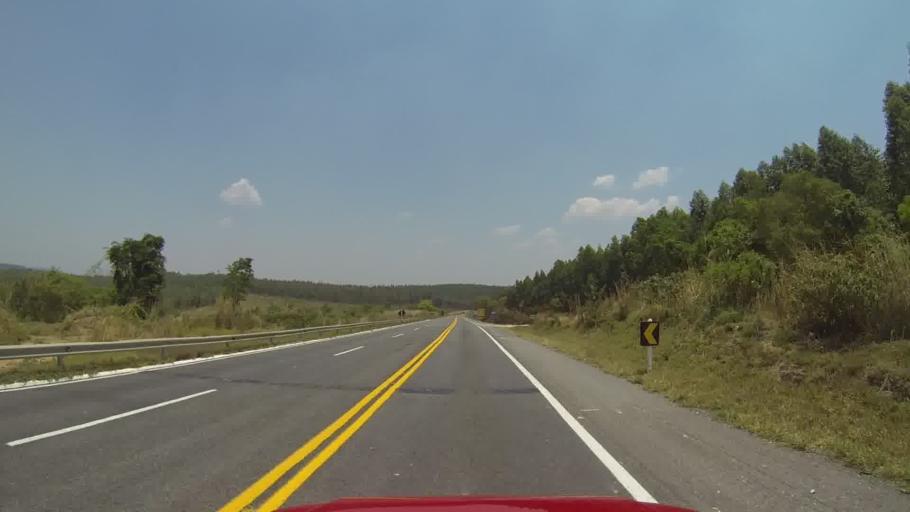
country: BR
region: Minas Gerais
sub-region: Formiga
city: Formiga
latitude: -20.3487
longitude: -45.3300
